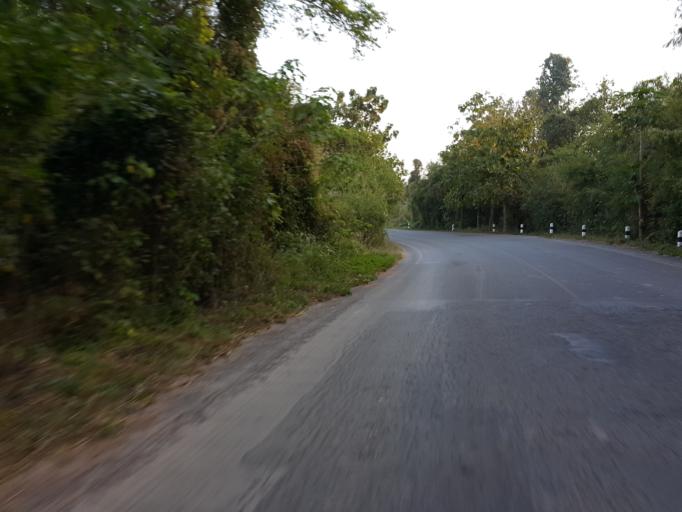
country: TH
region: Lamphun
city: Thung Hua Chang
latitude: 17.9319
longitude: 99.0477
